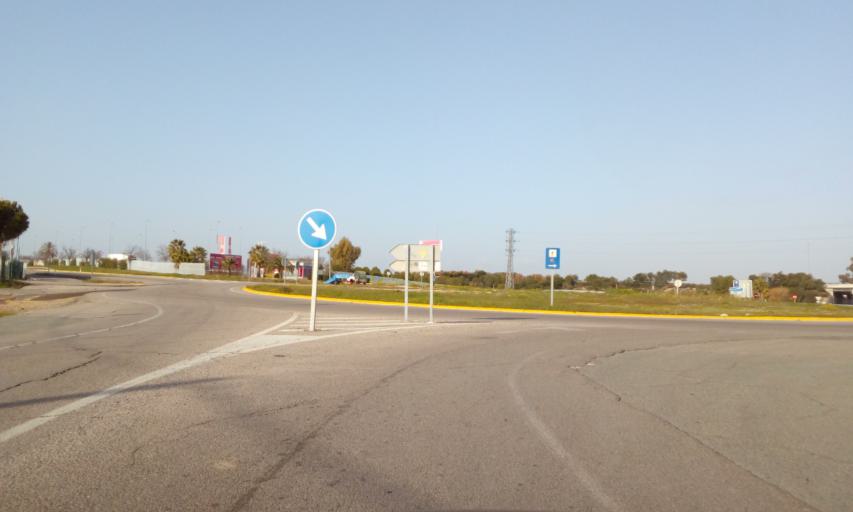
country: ES
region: Andalusia
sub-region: Provincia de Sevilla
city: Santiponce
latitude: 37.4546
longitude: -6.0463
